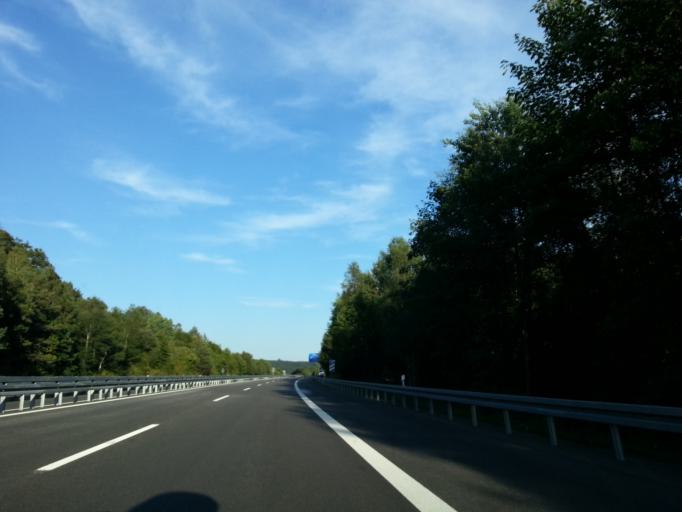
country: DE
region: Rheinland-Pfalz
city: Achtelsbach
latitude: 49.5870
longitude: 7.0779
